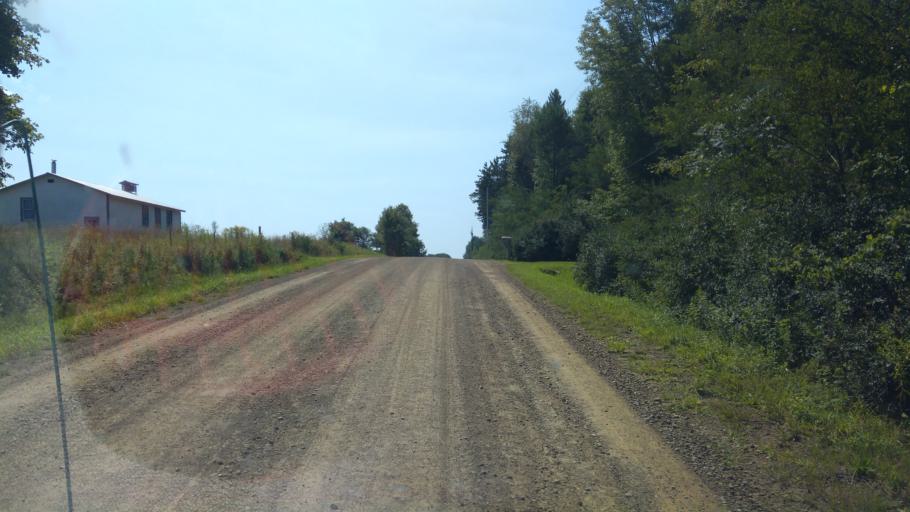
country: US
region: New York
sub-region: Allegany County
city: Houghton
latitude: 42.3577
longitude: -78.0408
